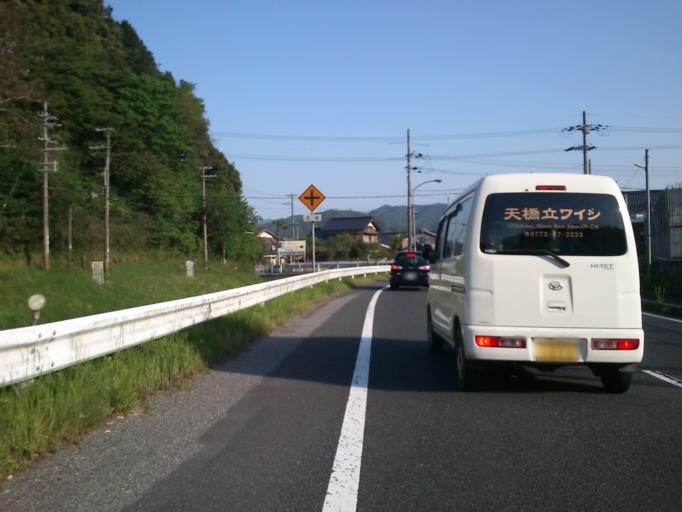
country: JP
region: Kyoto
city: Miyazu
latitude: 35.5758
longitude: 135.1603
